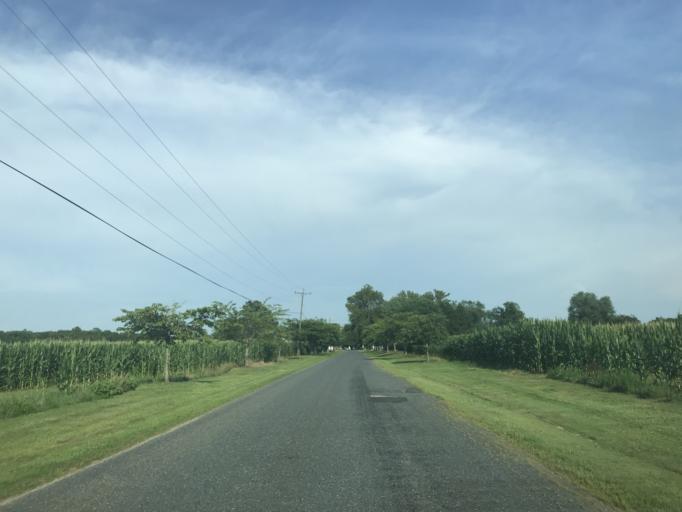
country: US
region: Maryland
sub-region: Harford County
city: Havre de Grace
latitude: 39.5208
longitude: -76.1140
